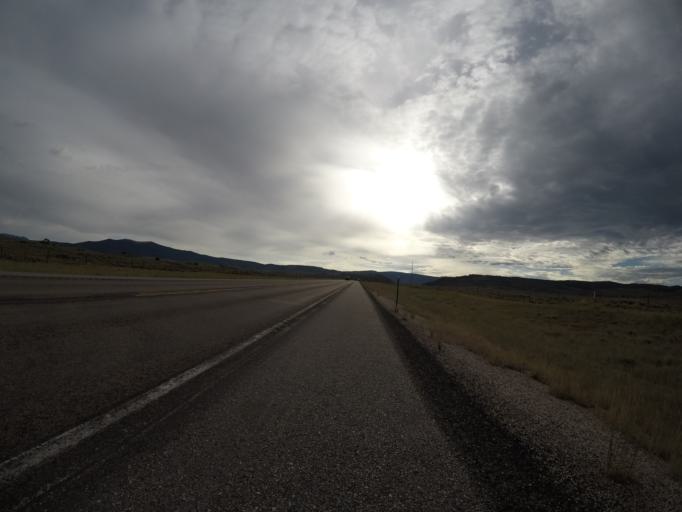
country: US
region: Wyoming
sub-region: Carbon County
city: Saratoga
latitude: 41.3557
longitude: -106.6029
